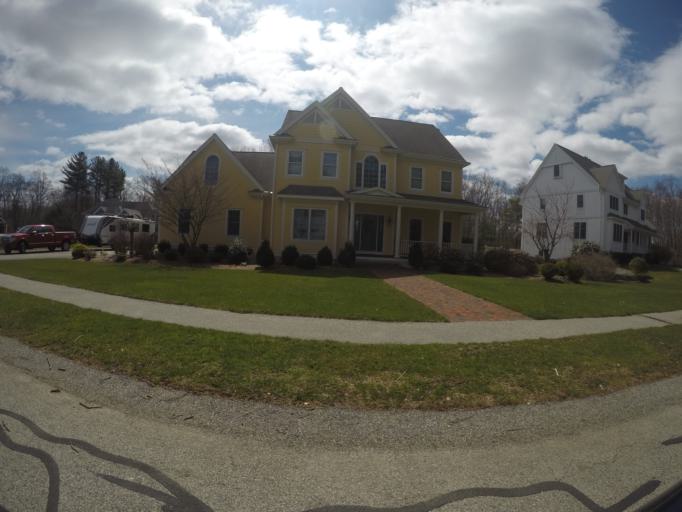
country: US
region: Massachusetts
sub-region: Bristol County
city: Easton
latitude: 42.0702
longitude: -71.1174
